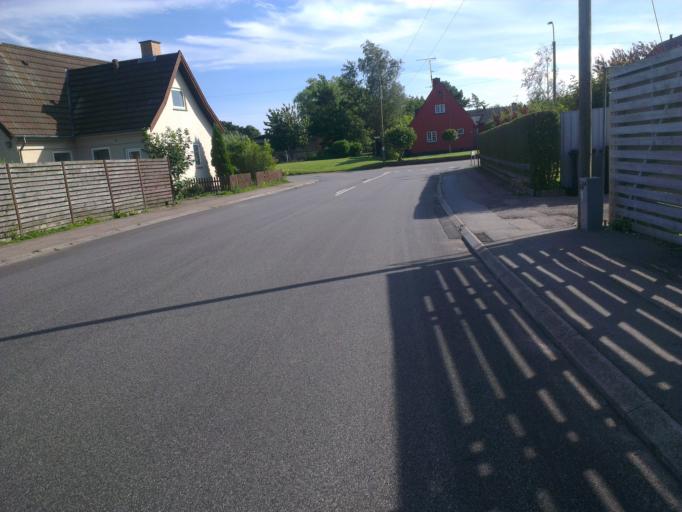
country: DK
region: Capital Region
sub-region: Frederikssund Kommune
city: Skibby
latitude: 55.7499
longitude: 11.9562
